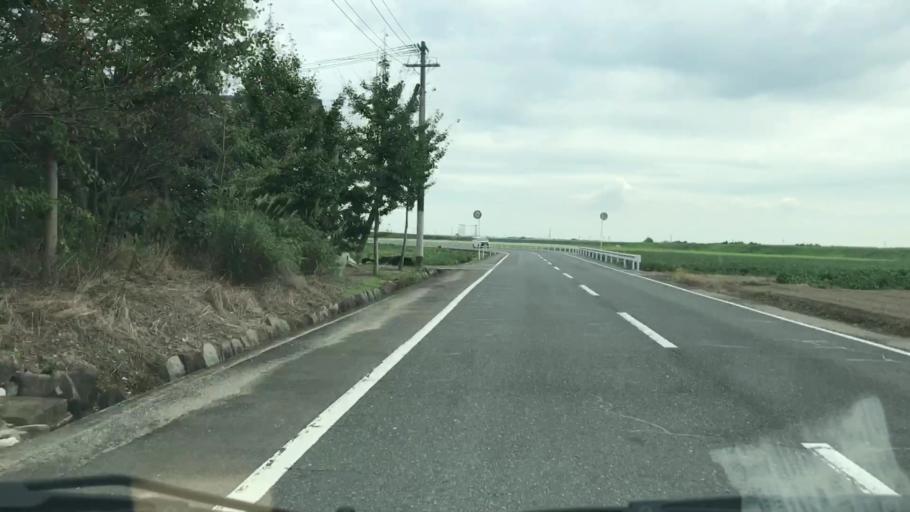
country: JP
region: Saga Prefecture
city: Saga-shi
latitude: 33.2904
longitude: 130.2400
